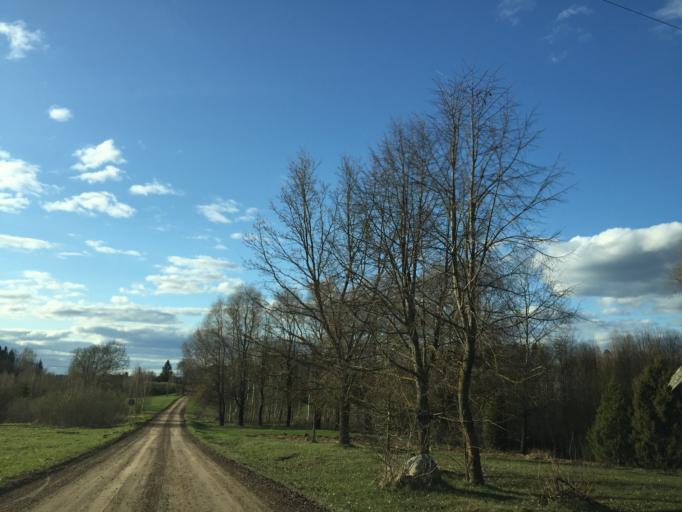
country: LV
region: Rezekne
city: Rezekne
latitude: 56.5767
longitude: 27.3605
